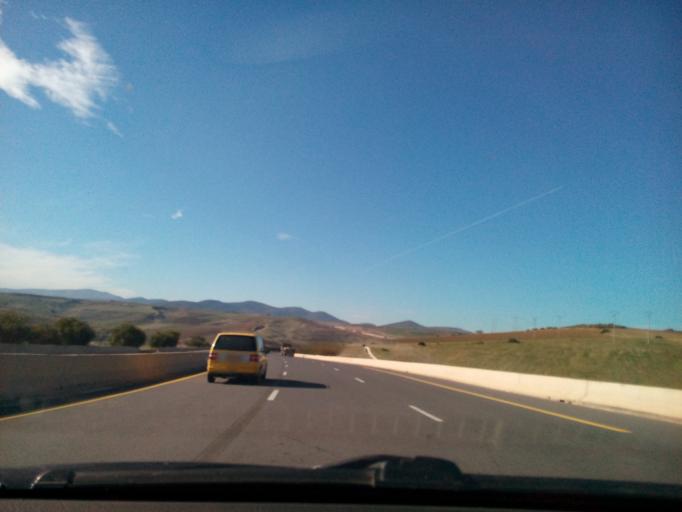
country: DZ
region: Tlemcen
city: Sidi Abdelli
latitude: 35.0397
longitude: -1.0460
